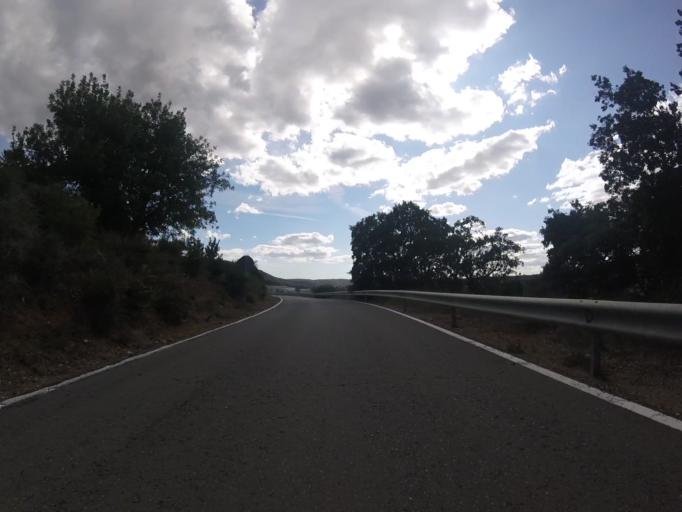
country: ES
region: Valencia
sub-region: Provincia de Castello
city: Cuevas de Vinroma
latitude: 40.3526
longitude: 0.1272
